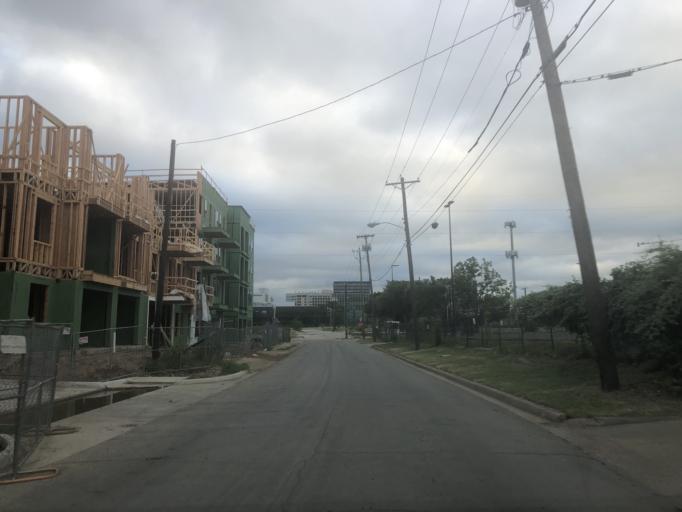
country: US
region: Texas
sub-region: Dallas County
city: University Park
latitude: 32.8267
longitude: -96.8507
